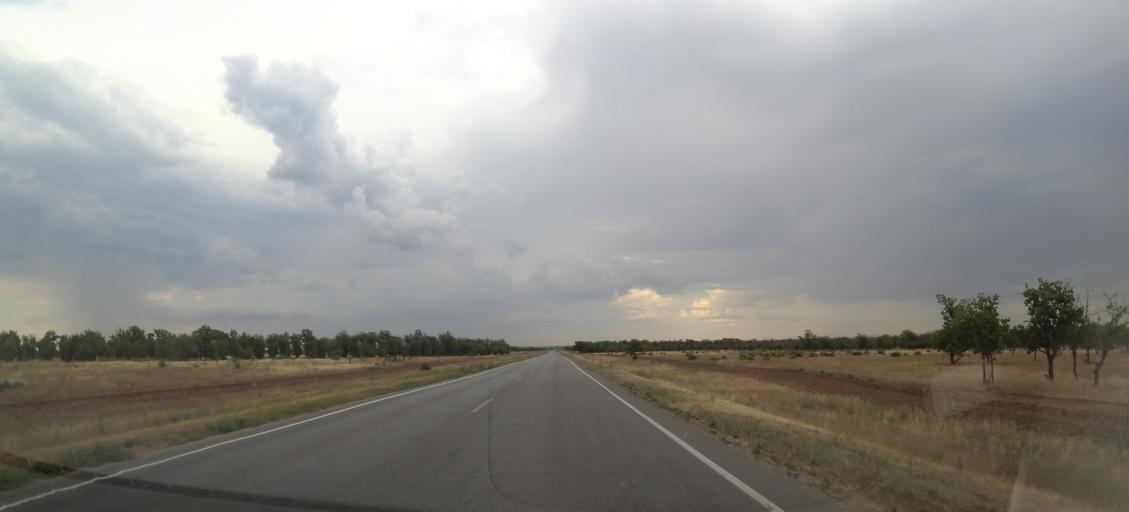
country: RU
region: Volgograd
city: Kotel'nikovo
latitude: 47.6113
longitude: 43.1106
